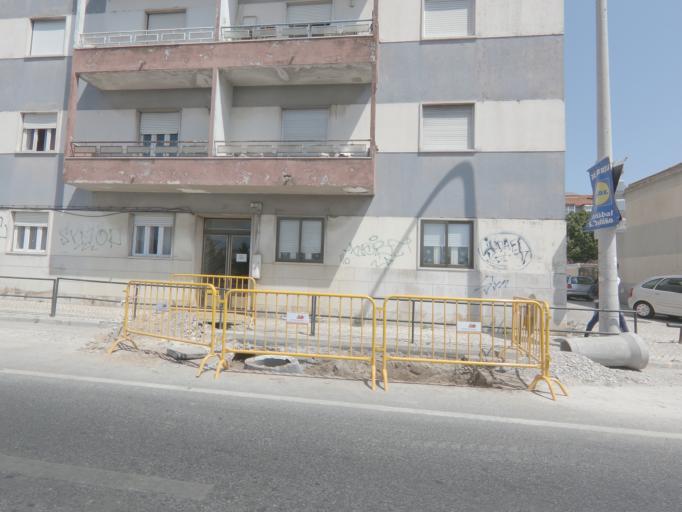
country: PT
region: Setubal
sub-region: Setubal
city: Setubal
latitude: 38.5353
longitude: -8.8844
